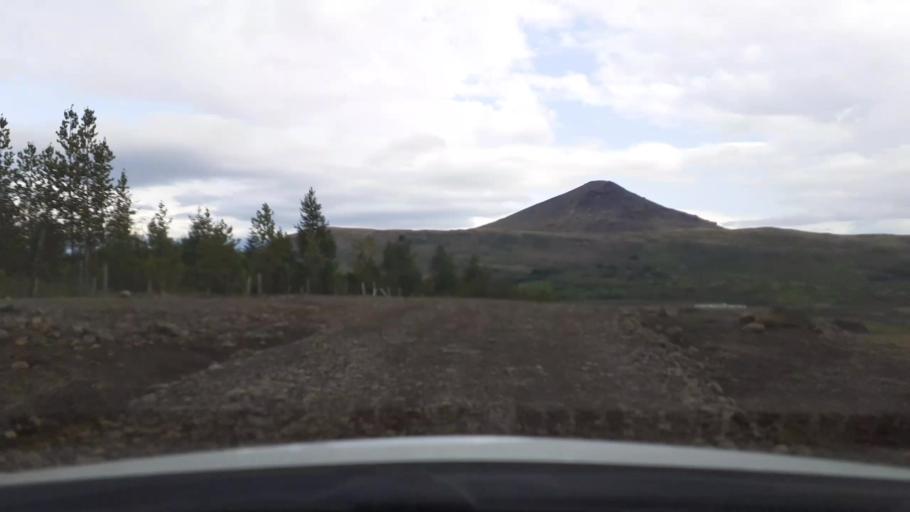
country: IS
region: Capital Region
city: Mosfellsbaer
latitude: 64.2887
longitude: -21.4610
